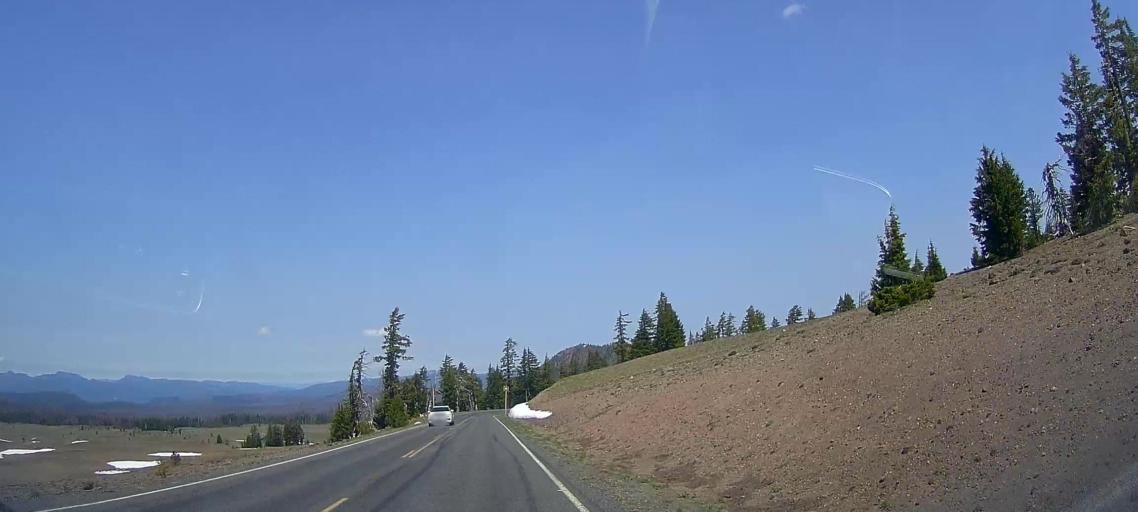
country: US
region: Oregon
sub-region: Jackson County
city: Shady Cove
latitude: 42.9705
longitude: -122.1522
